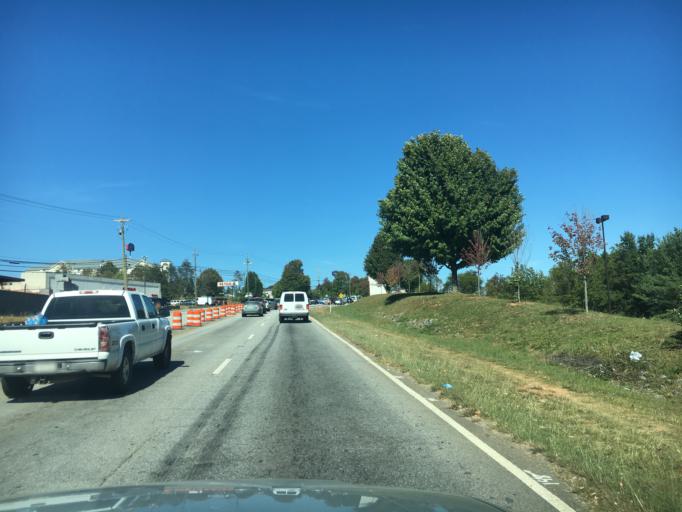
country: US
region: North Carolina
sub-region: Buncombe County
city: Bent Creek
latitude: 35.5311
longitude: -82.6053
